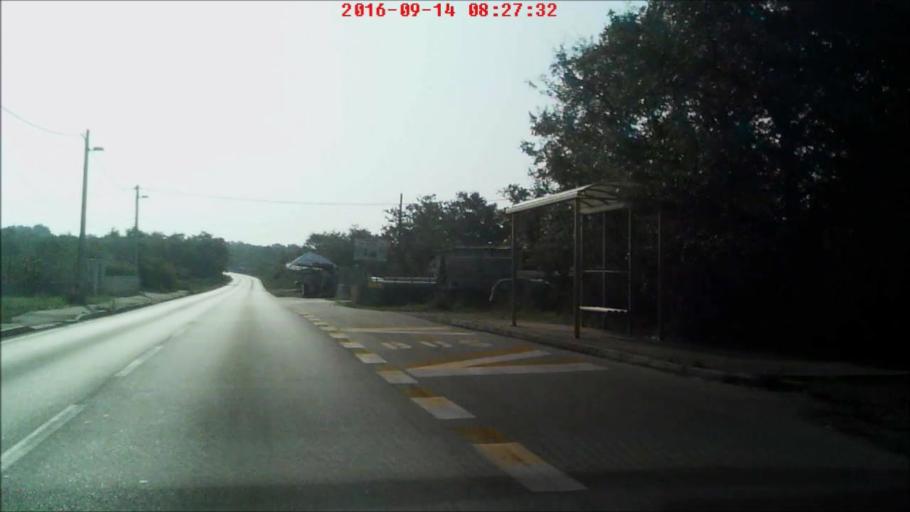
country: HR
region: Zadarska
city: Zadar
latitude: 44.1882
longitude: 15.2672
